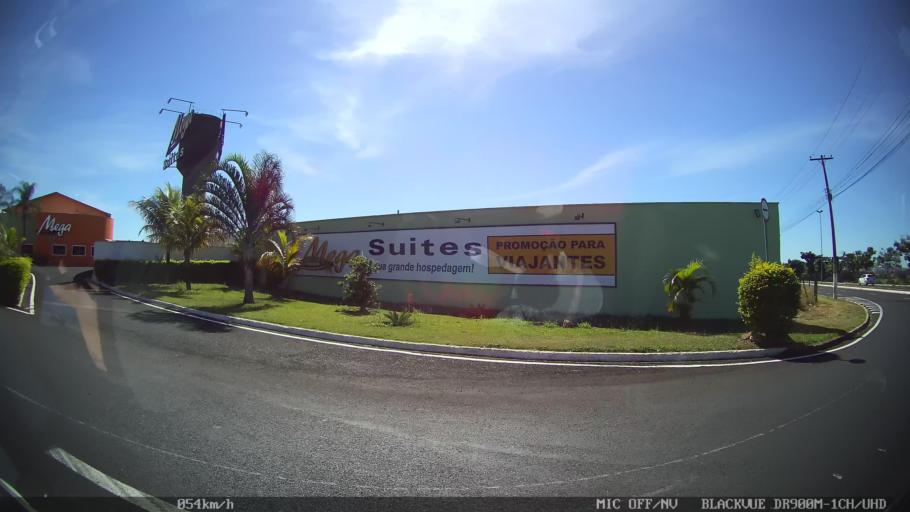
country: BR
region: Sao Paulo
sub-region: Franca
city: Franca
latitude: -20.5482
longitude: -47.4272
